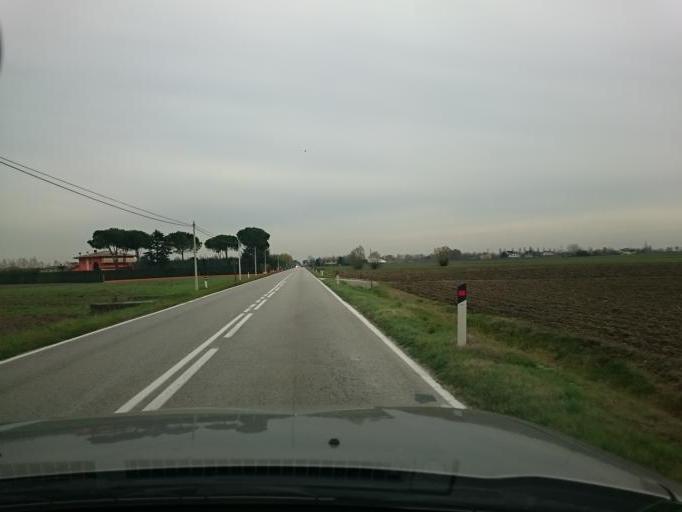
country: IT
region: Veneto
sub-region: Provincia di Padova
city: Due Carrare
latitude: 45.2982
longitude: 11.8468
